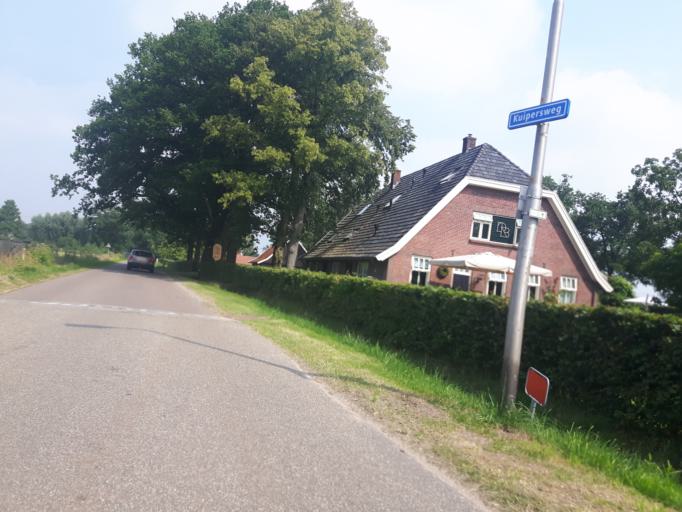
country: NL
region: Overijssel
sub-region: Gemeente Borne
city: Borne
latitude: 52.2990
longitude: 6.7139
